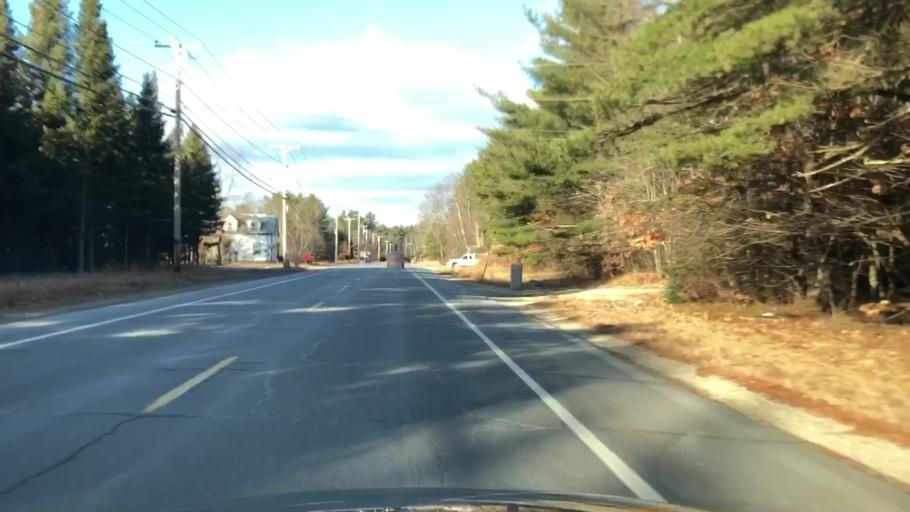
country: US
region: New Hampshire
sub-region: Hillsborough County
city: Brookline
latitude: 42.7651
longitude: -71.6743
